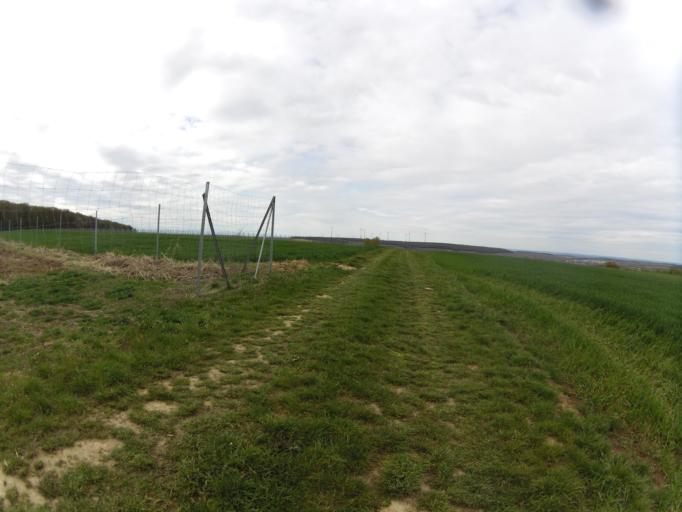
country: DE
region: Bavaria
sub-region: Regierungsbezirk Unterfranken
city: Nordheim
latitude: 49.8586
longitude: 10.1601
